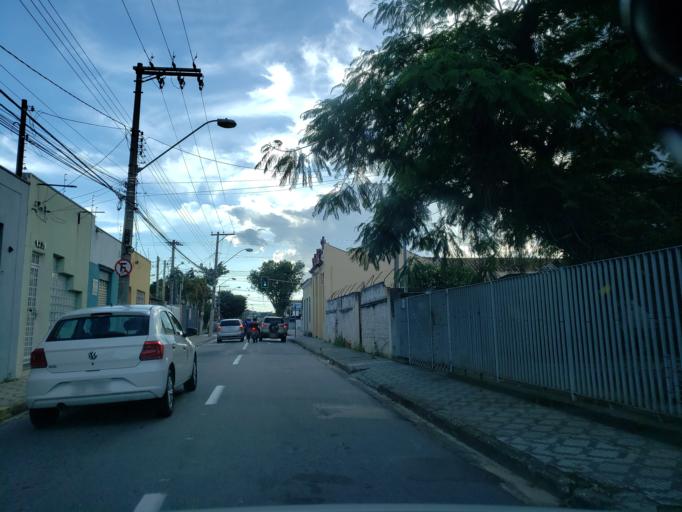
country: BR
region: Sao Paulo
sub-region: Taubate
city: Taubate
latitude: -23.0363
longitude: -45.5667
